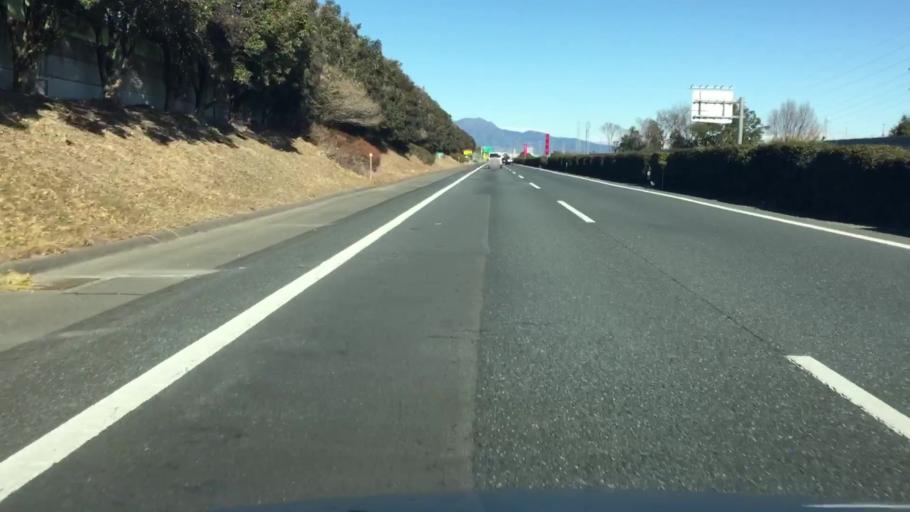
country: JP
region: Gunma
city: Maebashi-shi
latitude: 36.3814
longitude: 139.0268
